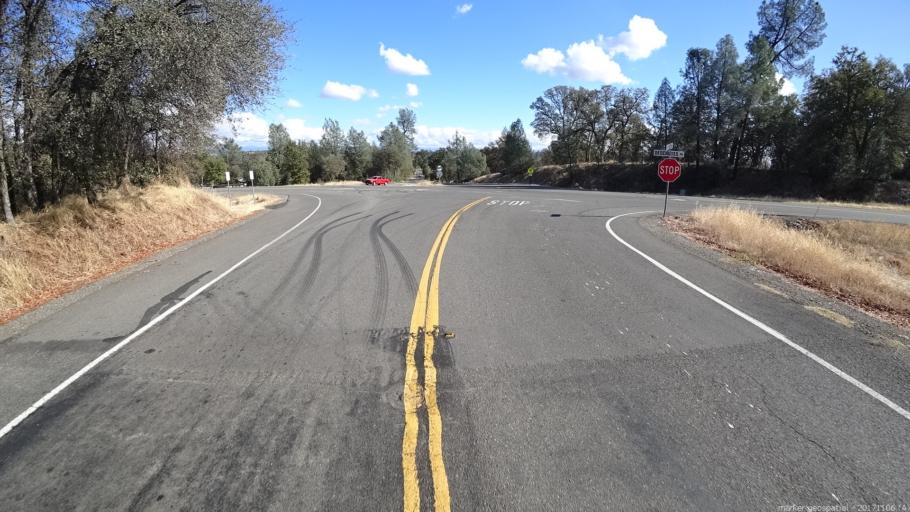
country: US
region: California
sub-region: Shasta County
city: Palo Cedro
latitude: 40.5928
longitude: -122.2386
